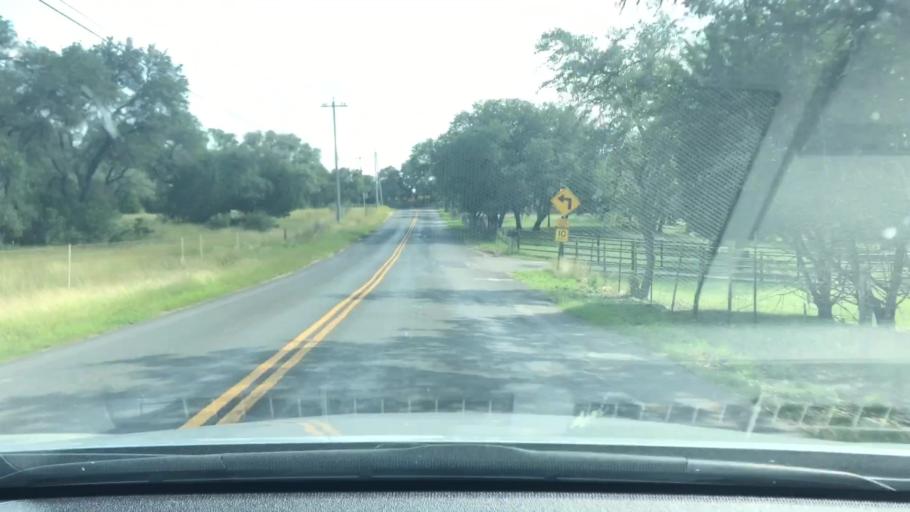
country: US
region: Texas
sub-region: Bexar County
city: Fair Oaks Ranch
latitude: 29.7722
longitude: -98.6263
